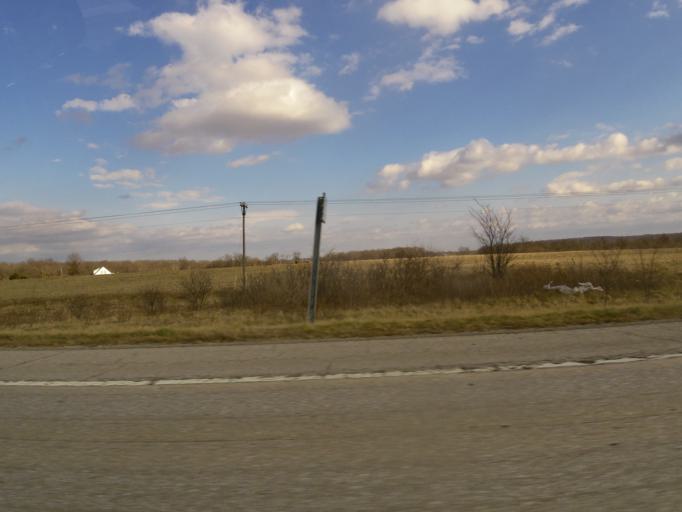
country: US
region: Missouri
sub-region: Pike County
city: Bowling Green
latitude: 39.2842
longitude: -91.1013
